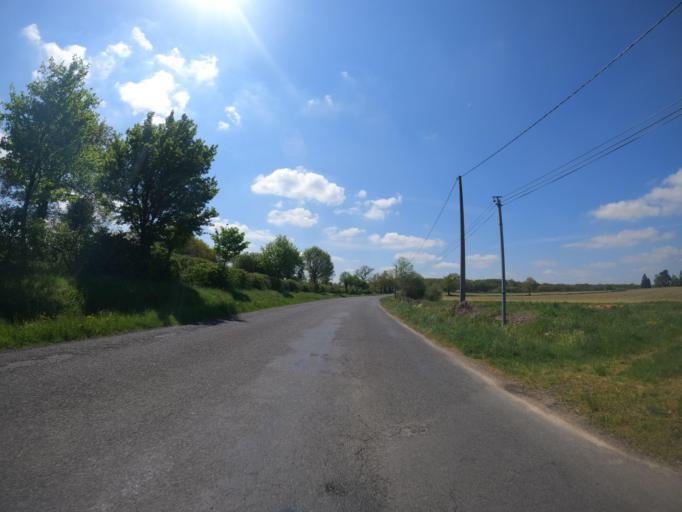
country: FR
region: Poitou-Charentes
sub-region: Departement des Deux-Sevres
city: Boisme
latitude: 46.7114
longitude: -0.4153
